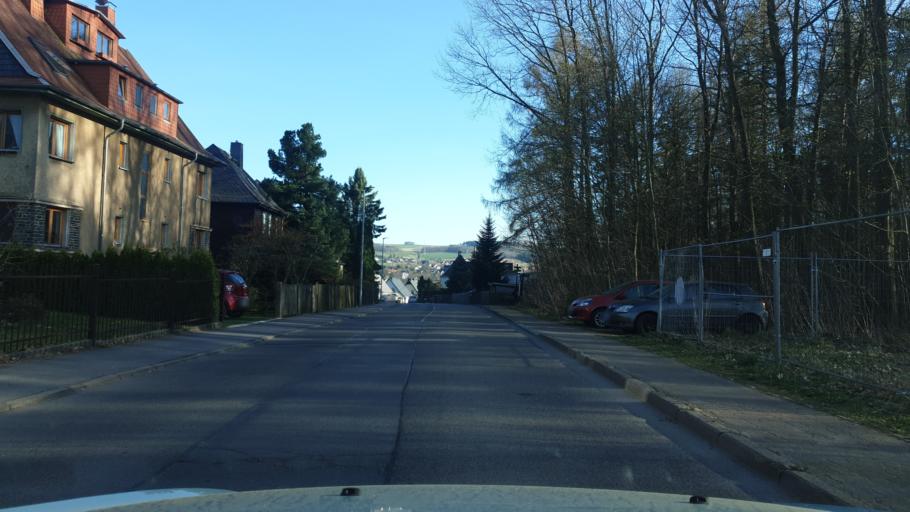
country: DE
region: Saxony
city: Neukirchen
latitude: 50.7797
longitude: 12.8985
